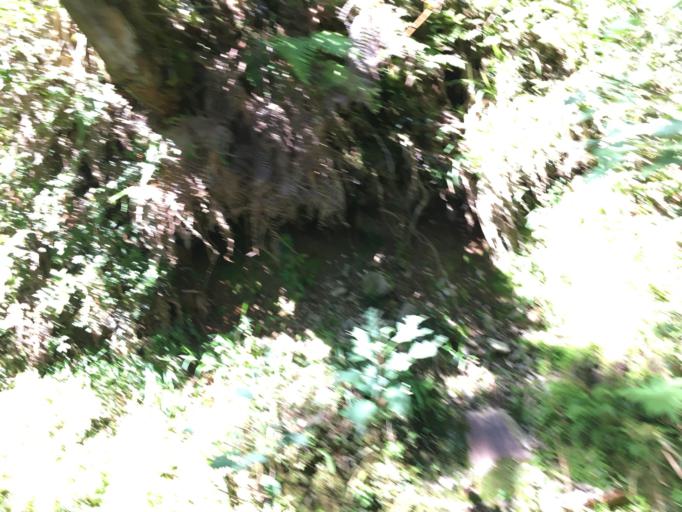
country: TW
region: Taiwan
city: Daxi
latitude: 24.5716
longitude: 121.4184
